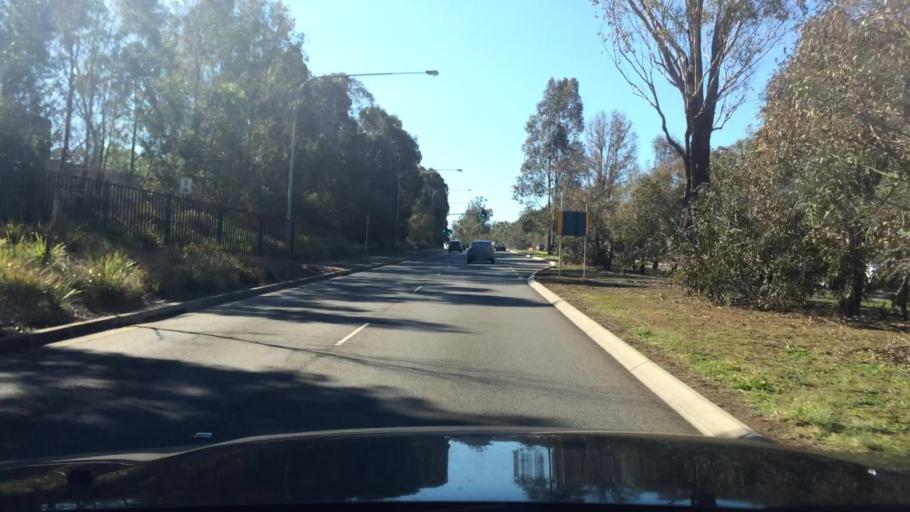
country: AU
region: New South Wales
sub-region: Fairfield
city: Cecil Park
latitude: -33.8904
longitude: 150.8597
